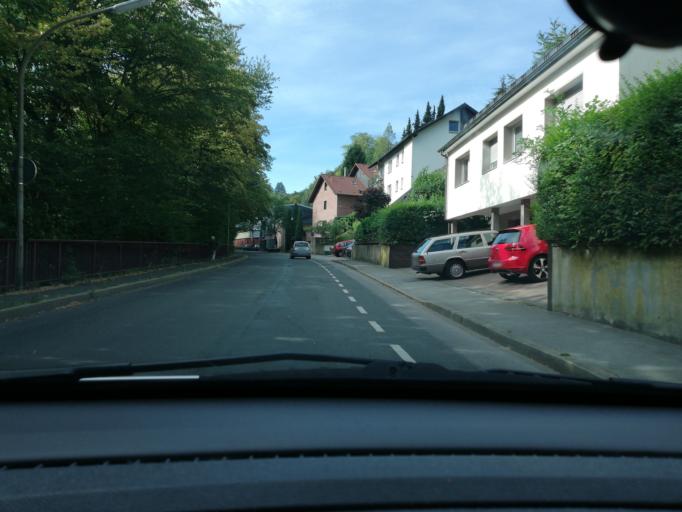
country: DE
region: North Rhine-Westphalia
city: Gevelsberg
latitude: 51.3123
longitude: 7.3379
